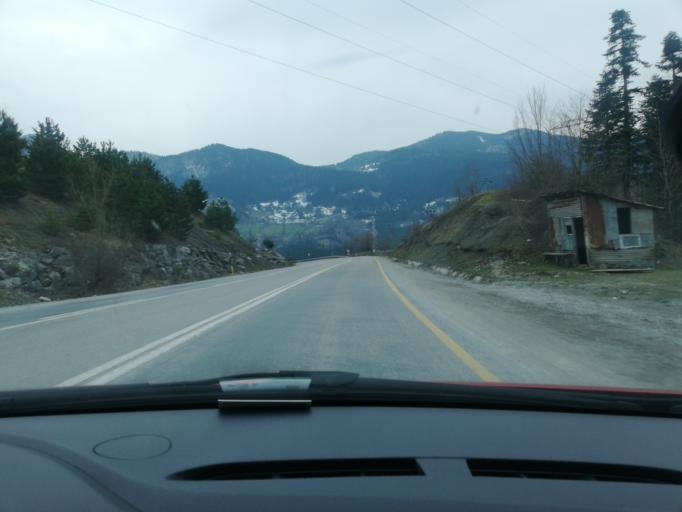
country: TR
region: Kastamonu
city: Kure
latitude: 41.8486
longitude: 33.7208
